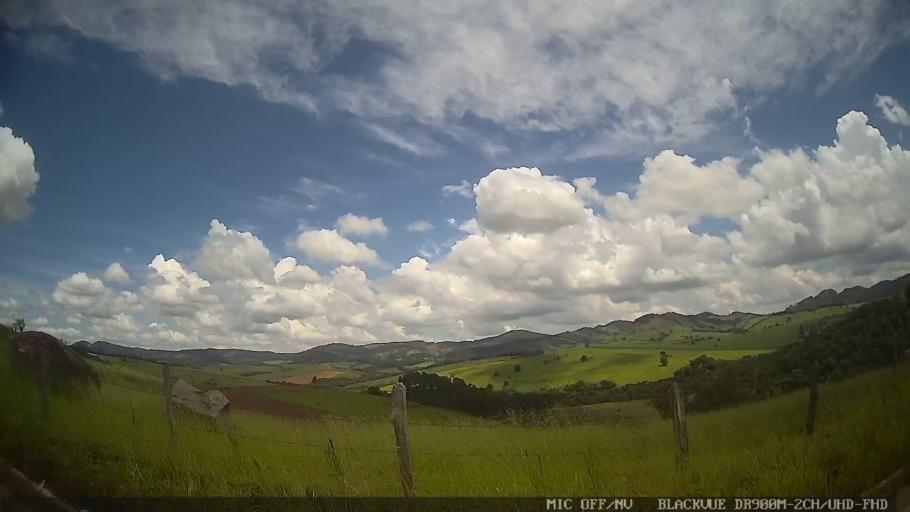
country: BR
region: Minas Gerais
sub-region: Extrema
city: Extrema
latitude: -22.7269
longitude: -46.4200
